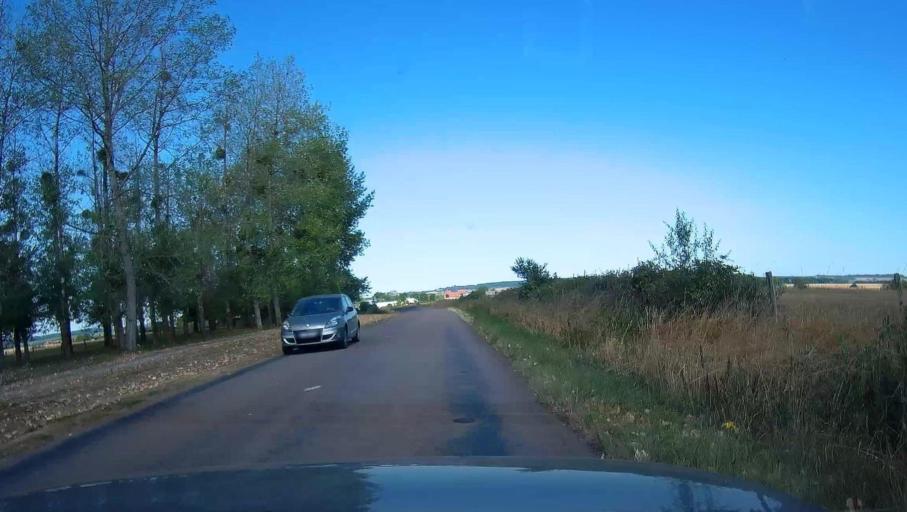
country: FR
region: Champagne-Ardenne
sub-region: Departement de la Haute-Marne
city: Langres
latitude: 47.8770
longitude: 5.3731
